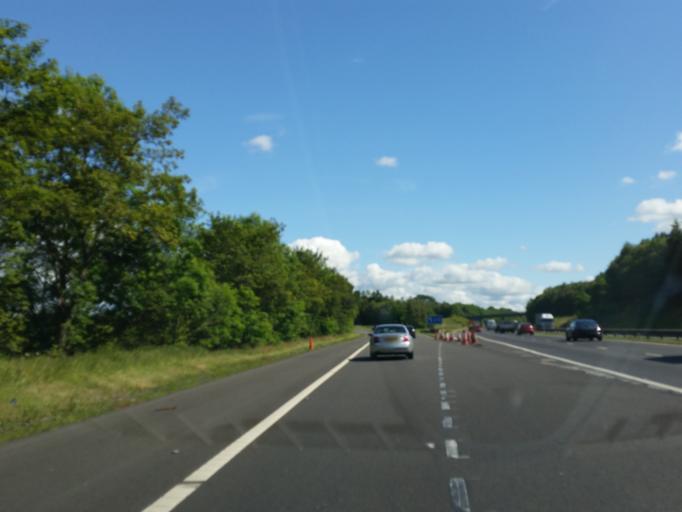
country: GB
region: Scotland
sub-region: South Lanarkshire
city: Larkhall
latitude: 55.7569
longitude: -3.9737
